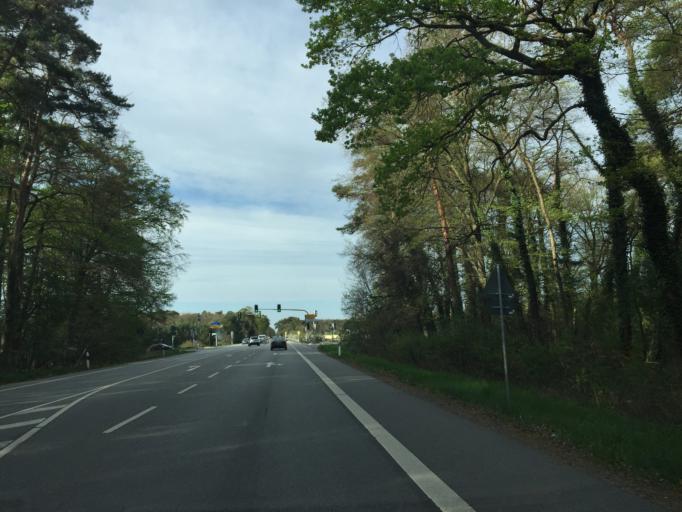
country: DE
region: Hesse
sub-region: Regierungsbezirk Darmstadt
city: Bickenbach
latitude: 49.7672
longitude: 8.6232
